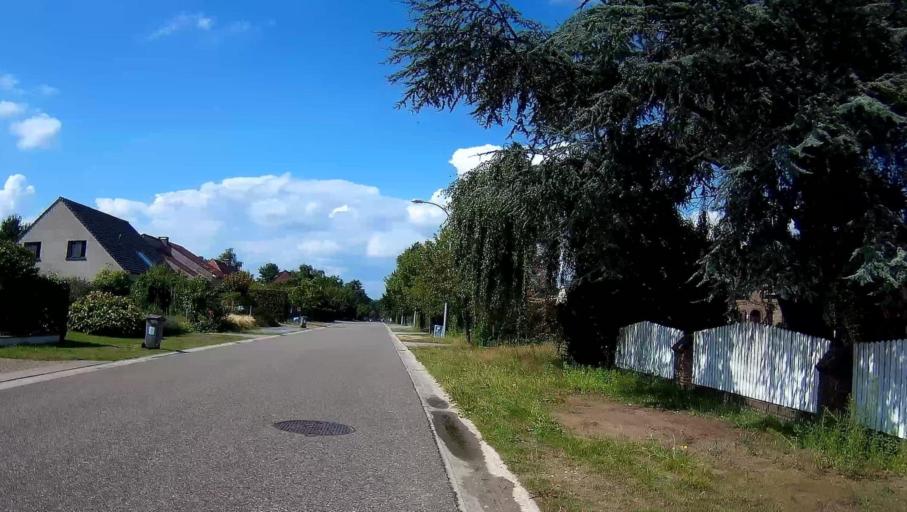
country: BE
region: Flanders
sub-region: Provincie Antwerpen
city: Balen
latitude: 51.1899
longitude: 5.2141
